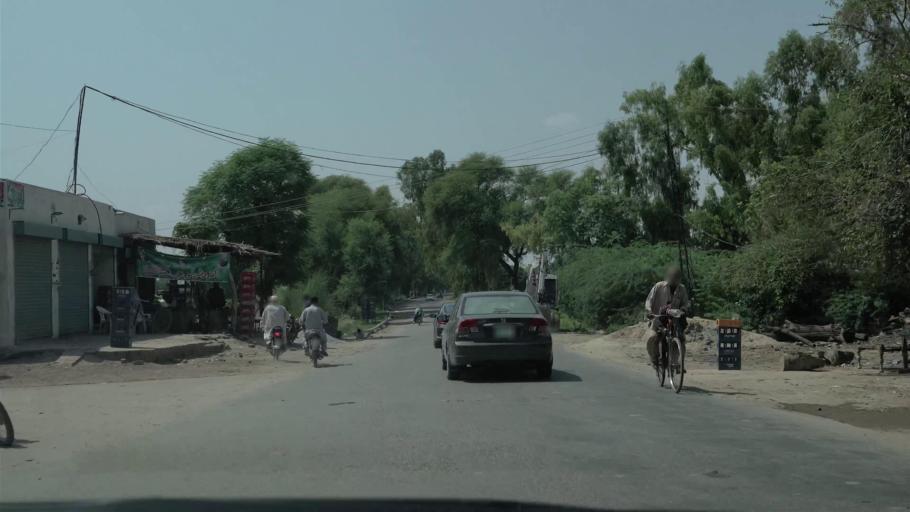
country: PK
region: Punjab
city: Gojra
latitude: 31.1698
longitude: 72.6226
